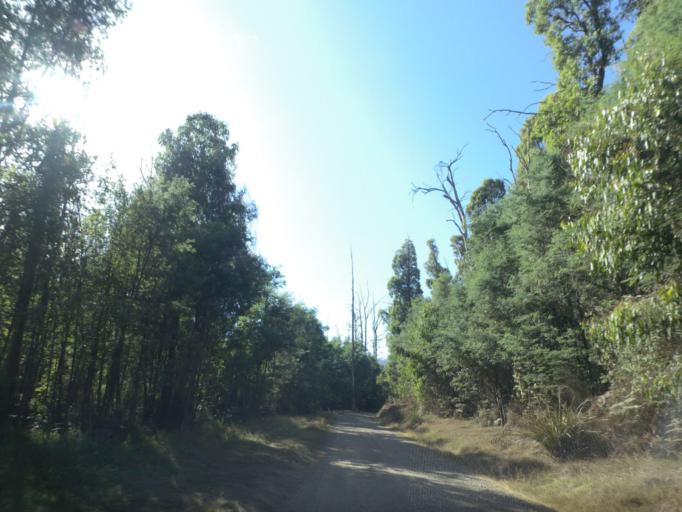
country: AU
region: Victoria
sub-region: Yarra Ranges
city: Millgrove
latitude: -37.5035
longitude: 145.7720
